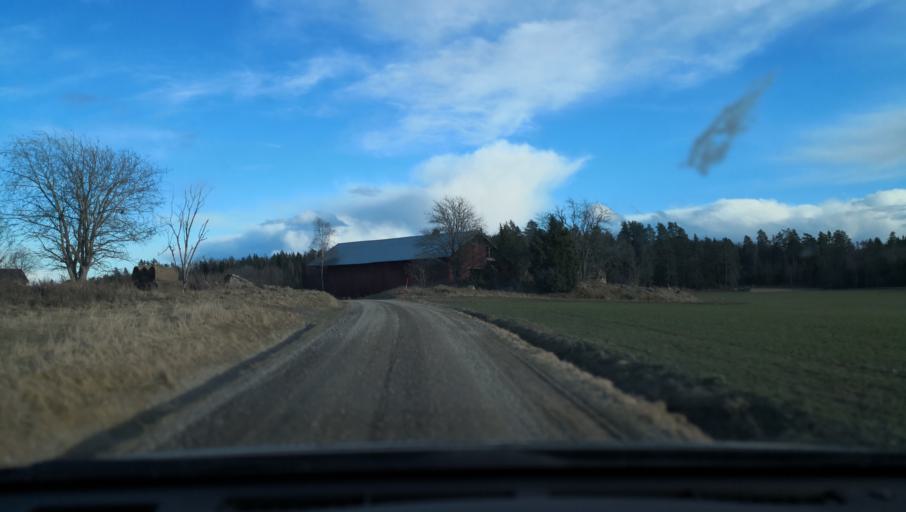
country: SE
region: Vaestmanland
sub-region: Arboga Kommun
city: Arboga
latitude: 59.4462
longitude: 15.7489
